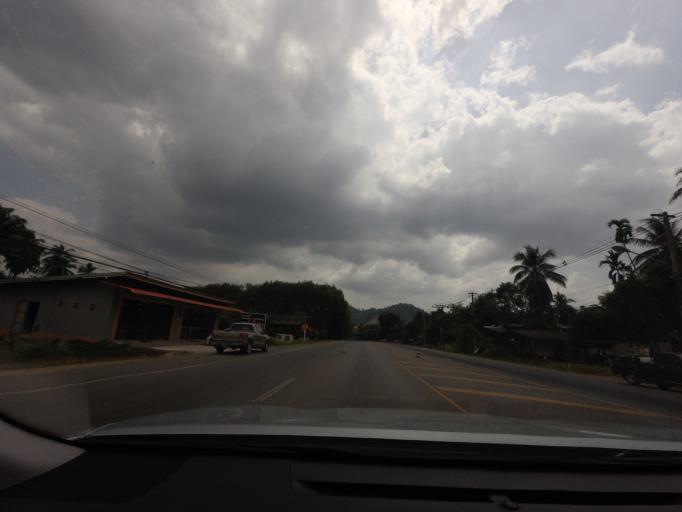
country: TH
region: Phangnga
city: Ban Ao Nang
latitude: 8.0962
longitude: 98.8038
